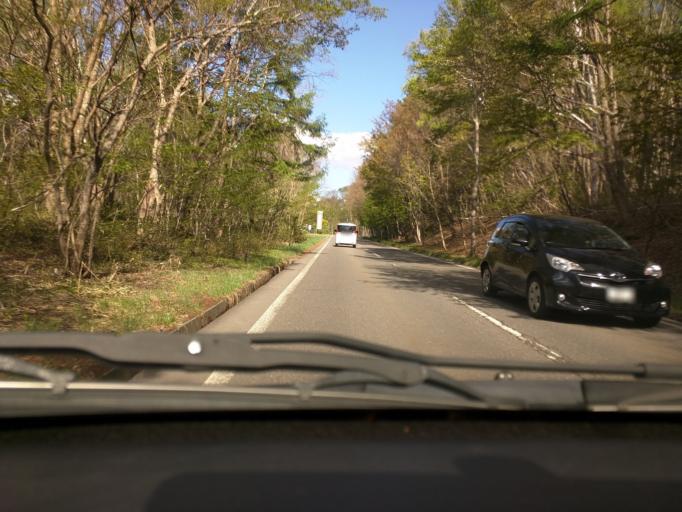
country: JP
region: Nagano
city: Nagano-shi
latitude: 36.7187
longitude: 138.1008
